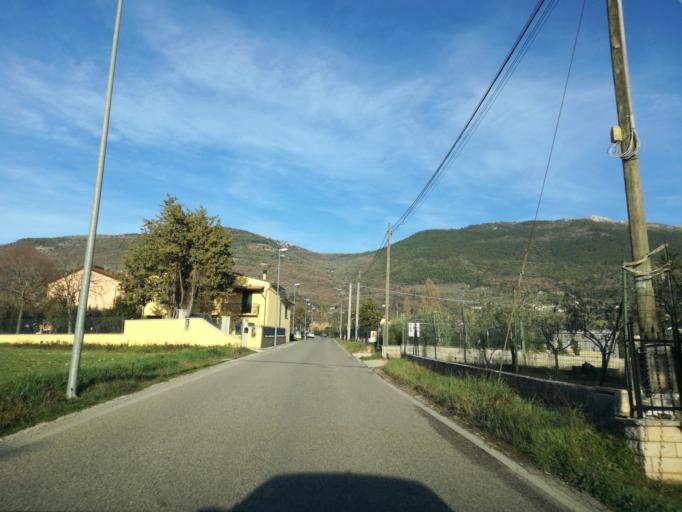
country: IT
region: Umbria
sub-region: Provincia di Perugia
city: Rivotorto
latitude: 43.0458
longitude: 12.6253
